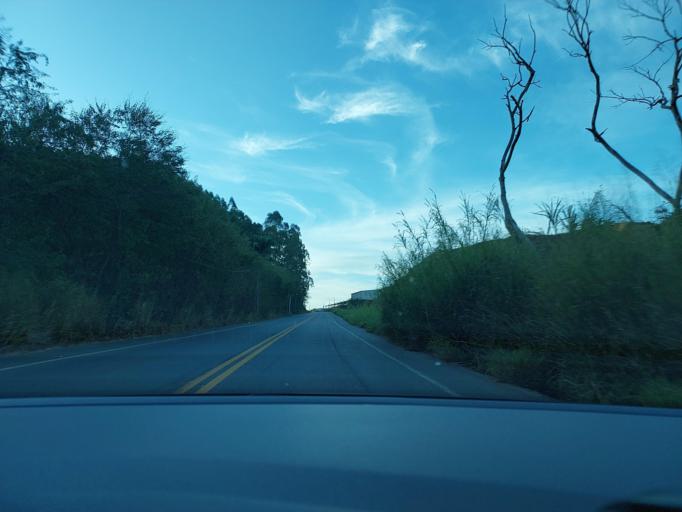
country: BR
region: Minas Gerais
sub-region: Vicosa
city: Vicosa
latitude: -20.8122
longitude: -42.8283
